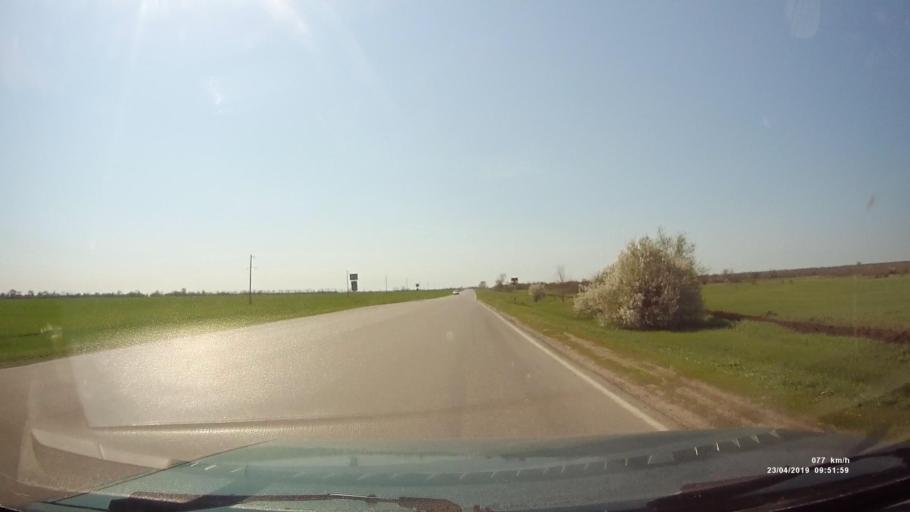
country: RU
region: Rostov
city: Orlovskiy
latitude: 46.8498
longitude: 42.0431
